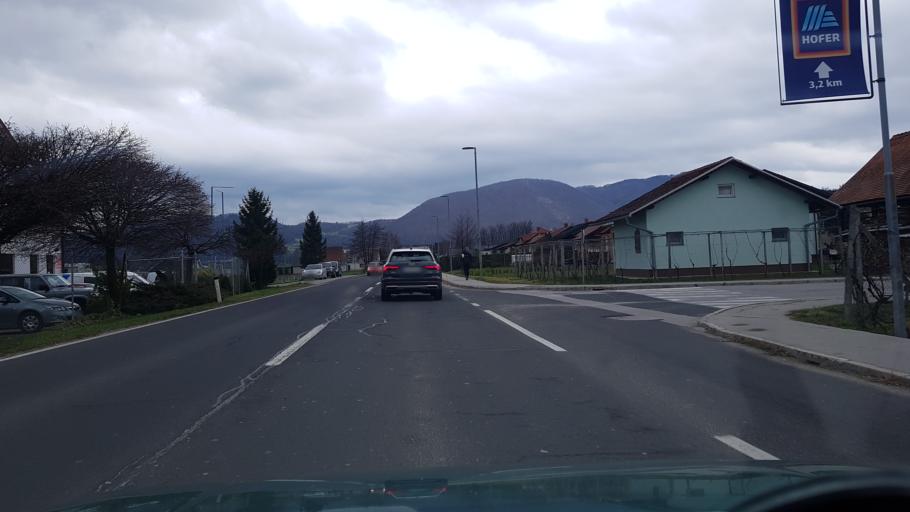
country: SI
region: Slovenska Konjice
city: Slovenske Konjice
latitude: 46.3442
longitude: 15.4732
